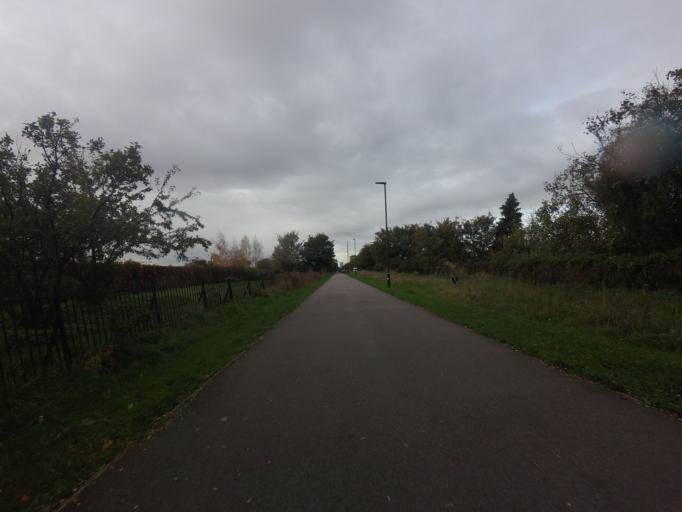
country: GB
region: England
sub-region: Greater London
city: East Ham
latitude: 51.5239
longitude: 0.0343
